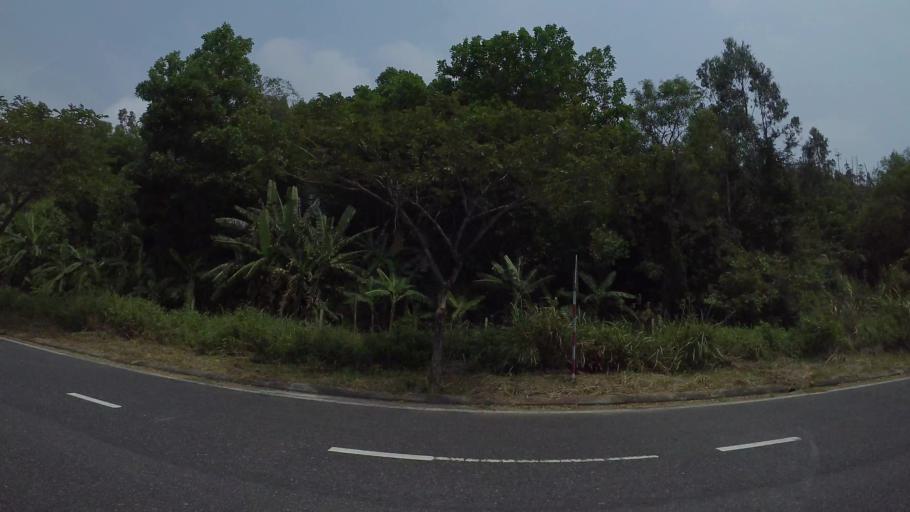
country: VN
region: Da Nang
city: Son Tra
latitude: 16.1044
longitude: 108.2641
